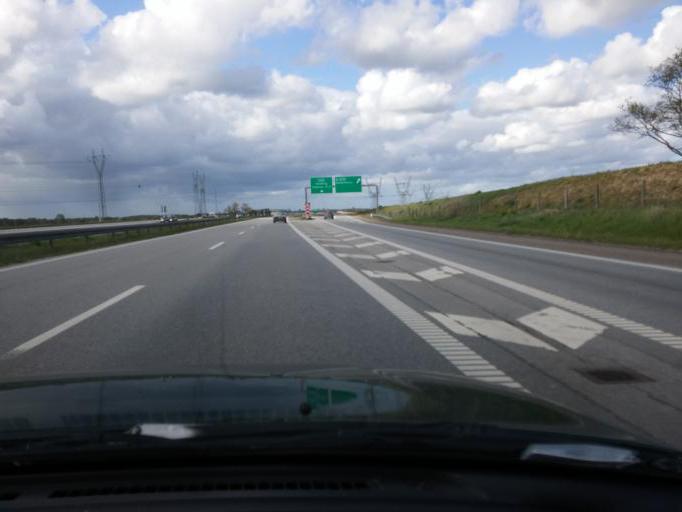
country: DK
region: South Denmark
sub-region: Odense Kommune
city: Hojby
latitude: 55.3429
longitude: 10.4542
